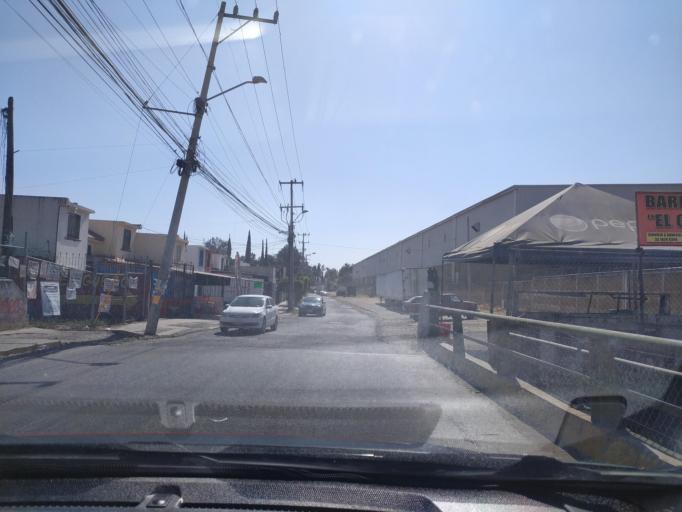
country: MX
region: Jalisco
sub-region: San Pedro Tlaquepaque
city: Paseo del Prado
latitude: 20.5825
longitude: -103.3868
